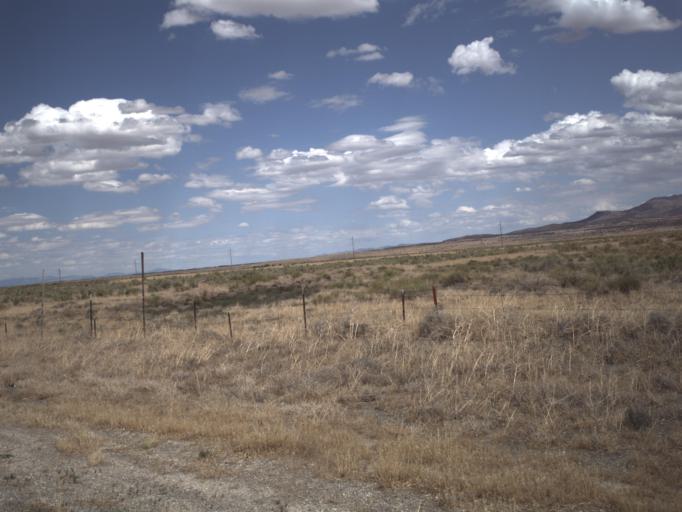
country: US
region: Utah
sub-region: Millard County
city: Delta
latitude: 39.2365
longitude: -112.4306
